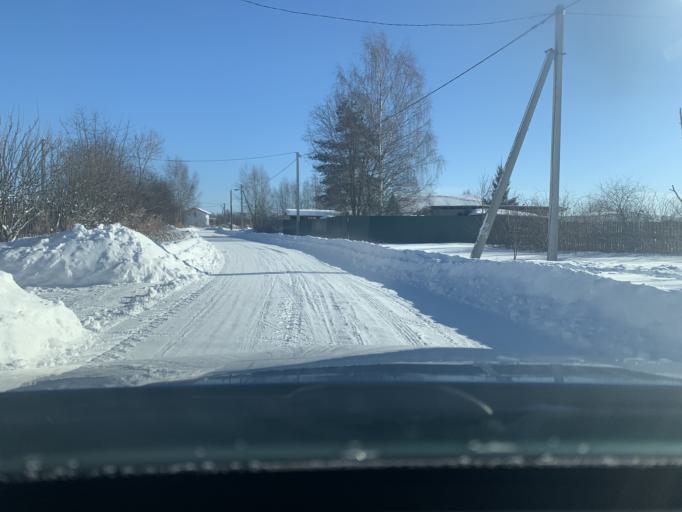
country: RU
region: Jaroslavl
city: Tunoshna
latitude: 57.6511
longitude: 40.0654
